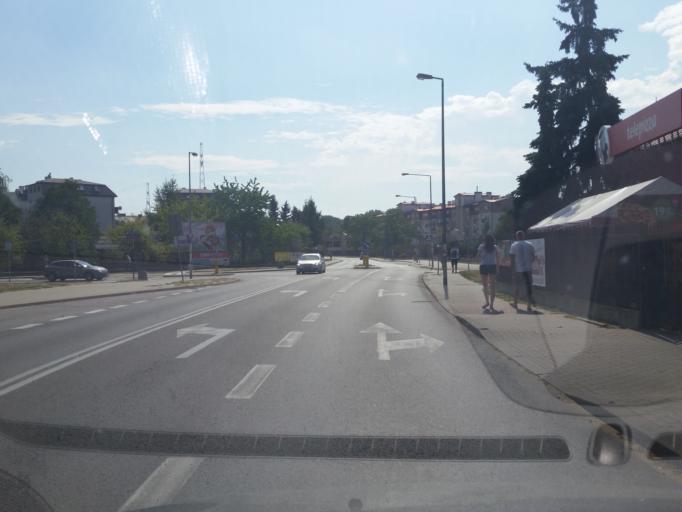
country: PL
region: Masovian Voivodeship
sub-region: Warszawa
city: Bialoleka
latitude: 52.3334
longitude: 20.9363
